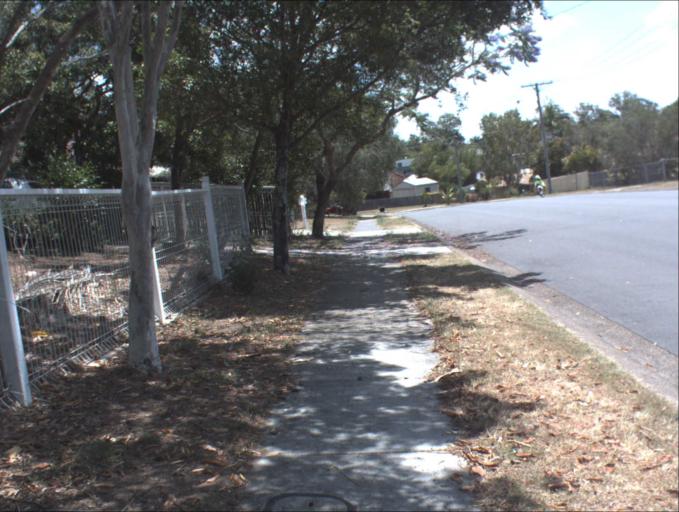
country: AU
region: Queensland
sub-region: Logan
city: Beenleigh
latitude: -27.7071
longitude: 153.2094
